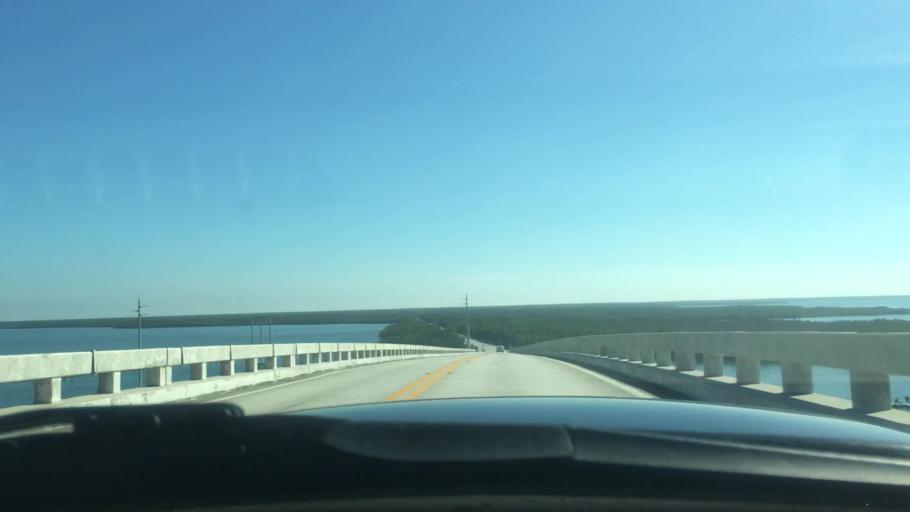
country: US
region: Florida
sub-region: Monroe County
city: North Key Largo
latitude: 25.2870
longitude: -80.3680
